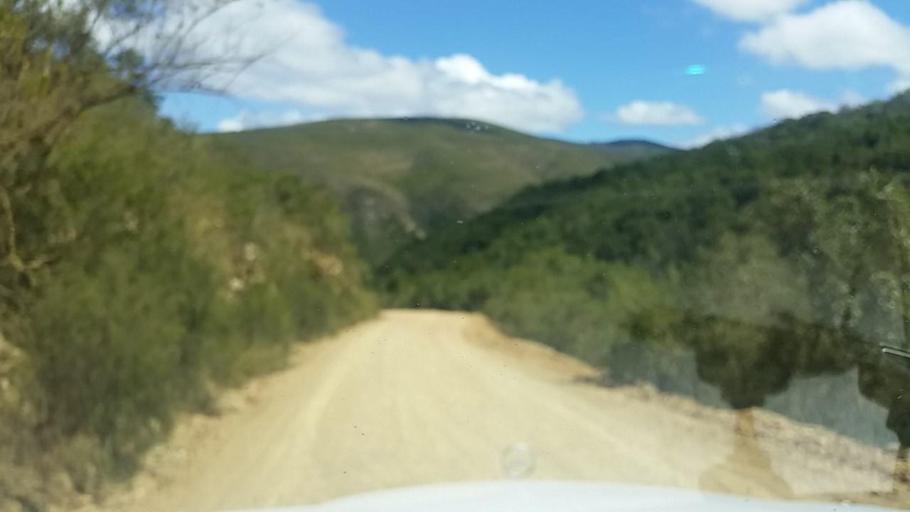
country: ZA
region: Western Cape
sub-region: Eden District Municipality
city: Knysna
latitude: -33.8581
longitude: 23.1800
